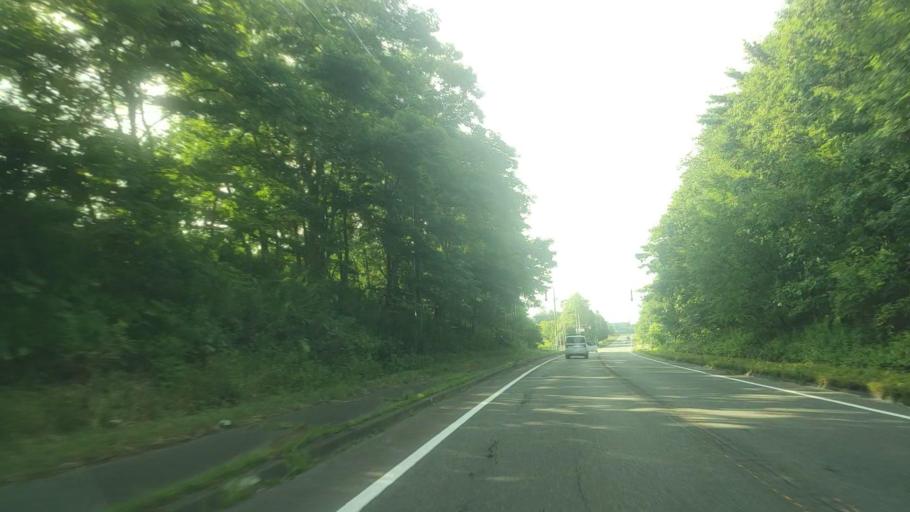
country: JP
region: Hokkaido
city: Chitose
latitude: 42.8788
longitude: 141.8163
